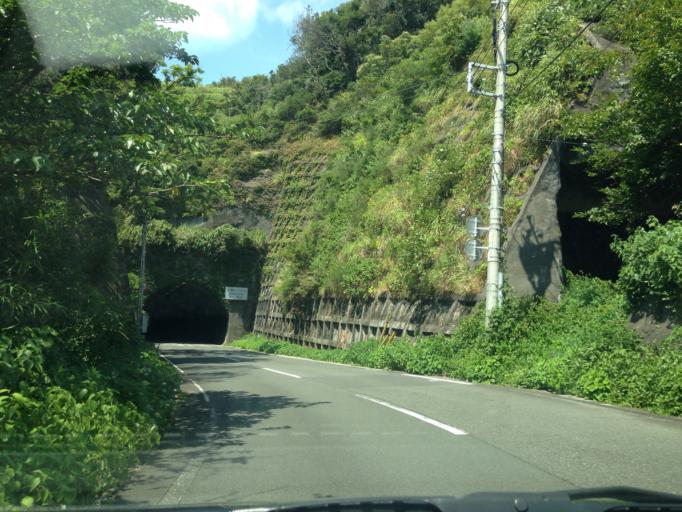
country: JP
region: Shizuoka
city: Shimoda
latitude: 34.6152
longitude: 138.8273
